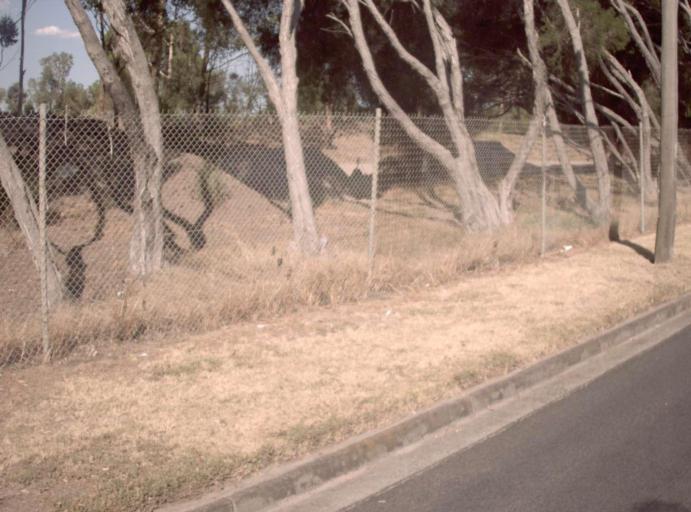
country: AU
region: Victoria
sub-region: Monash
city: Oakleigh South
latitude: -37.9360
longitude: 145.0876
